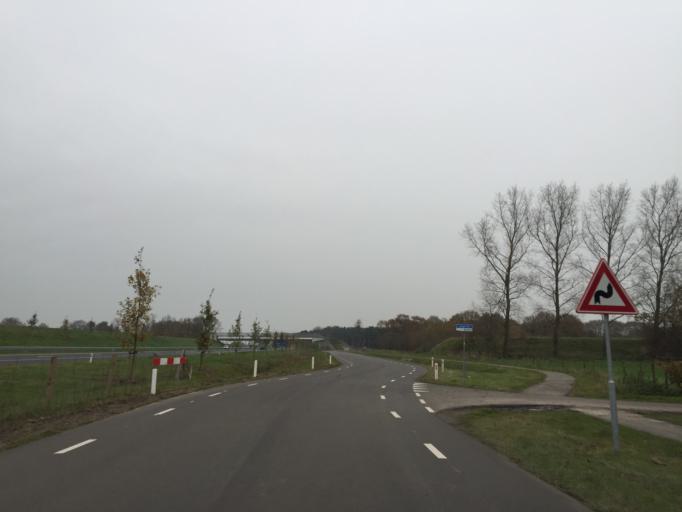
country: NL
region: North Brabant
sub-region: Gemeente Bergen op Zoom
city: Lepelstraat
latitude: 51.5481
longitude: 4.2957
